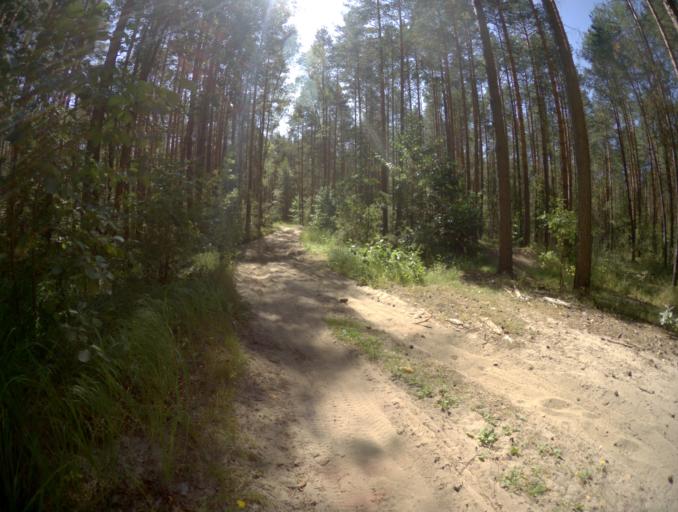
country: RU
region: Vladimir
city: Sobinka
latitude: 55.9482
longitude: 39.9937
